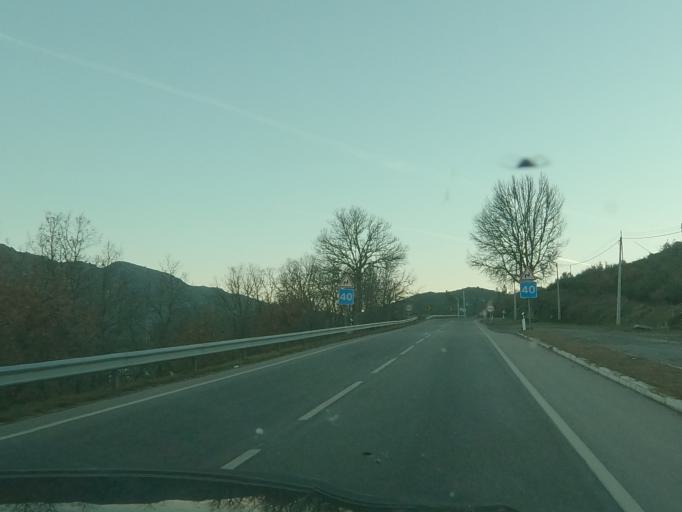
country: PT
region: Vila Real
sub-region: Vila Pouca de Aguiar
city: Vila Pouca de Aguiar
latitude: 41.4193
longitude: -7.6850
